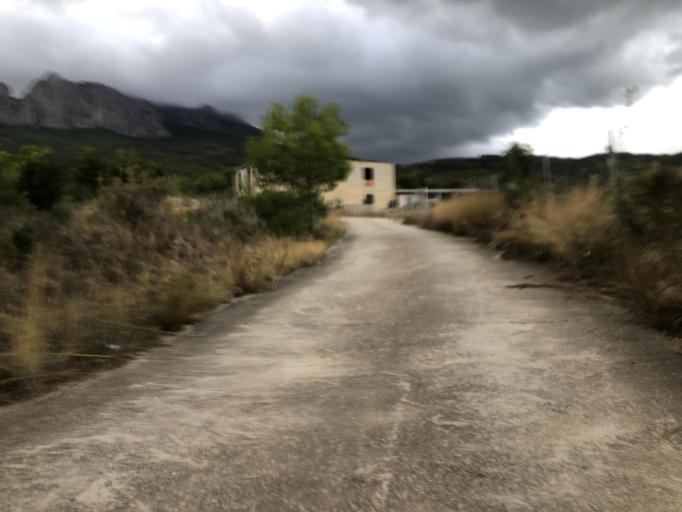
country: ES
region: Valencia
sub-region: Provincia de Alicante
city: Polop
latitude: 38.6364
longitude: -0.1515
